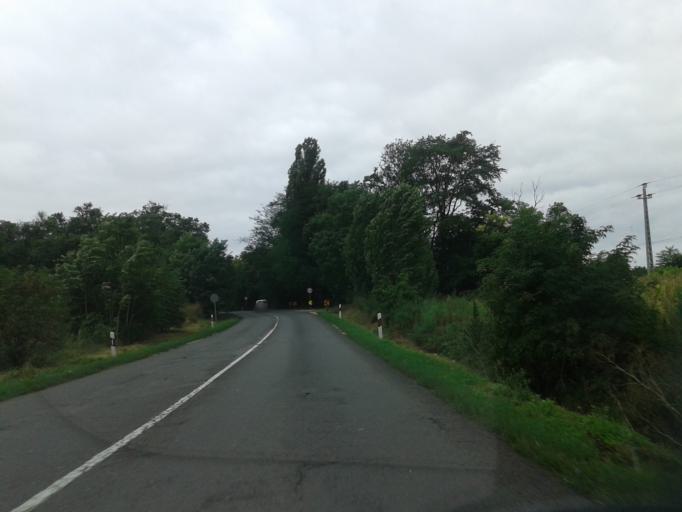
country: HU
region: Pest
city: Kiskunlachaza
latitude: 47.2415
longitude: 19.0208
